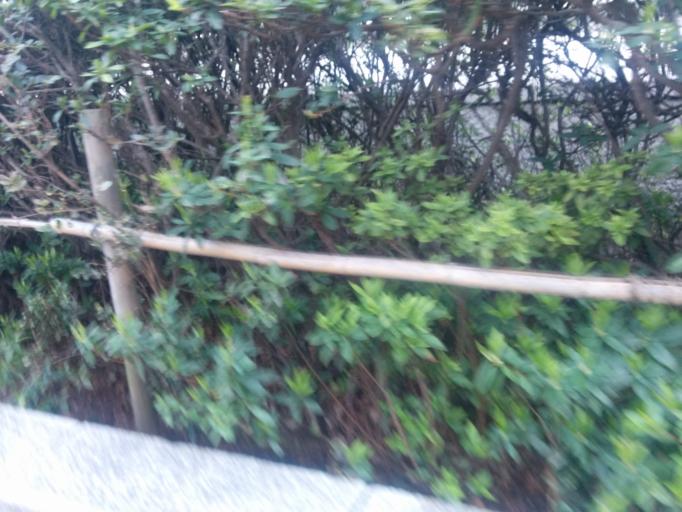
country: JP
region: Tokyo
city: Tokyo
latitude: 35.6921
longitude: 139.6942
